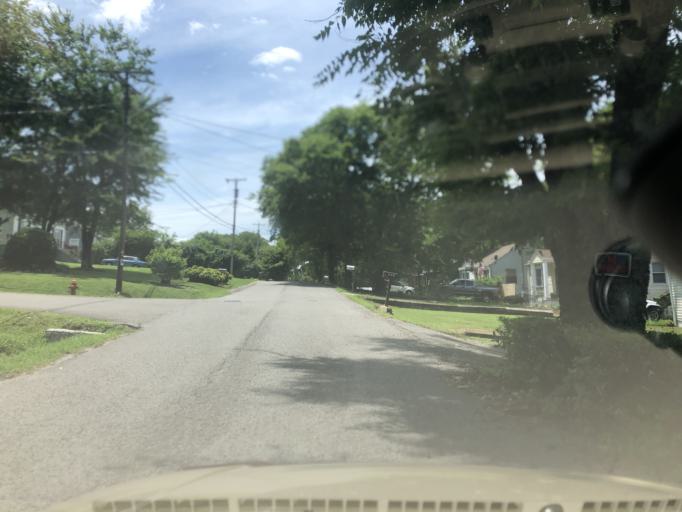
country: US
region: Tennessee
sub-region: Davidson County
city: Lakewood
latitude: 36.2575
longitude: -86.6993
